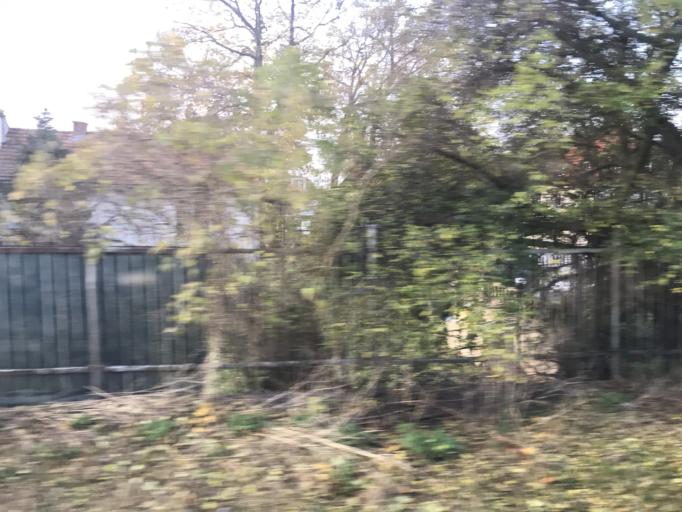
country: PL
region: Pomeranian Voivodeship
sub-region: Powiat pucki
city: Jastarnia
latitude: 54.7007
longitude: 18.6782
